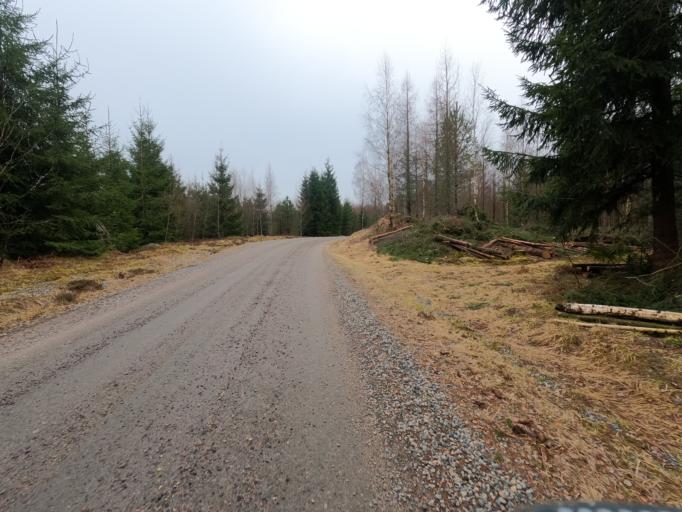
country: SE
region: Kronoberg
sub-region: Markaryds Kommun
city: Stromsnasbruk
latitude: 56.8131
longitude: 13.5699
